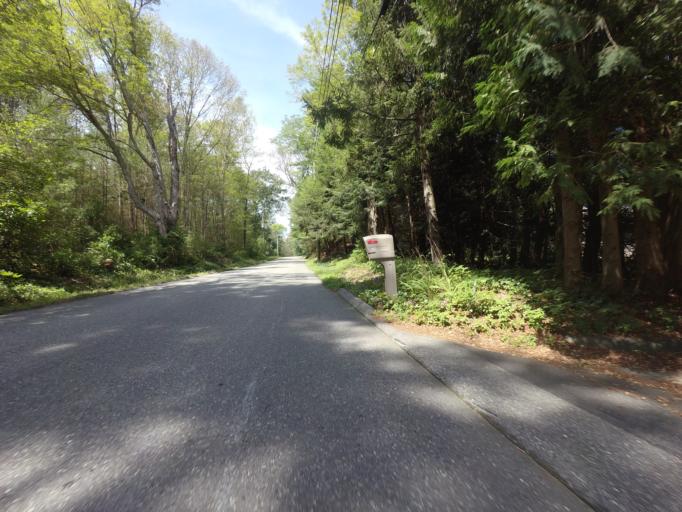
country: US
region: Connecticut
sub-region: Windham County
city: East Brooklyn
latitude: 41.8286
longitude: -71.9341
